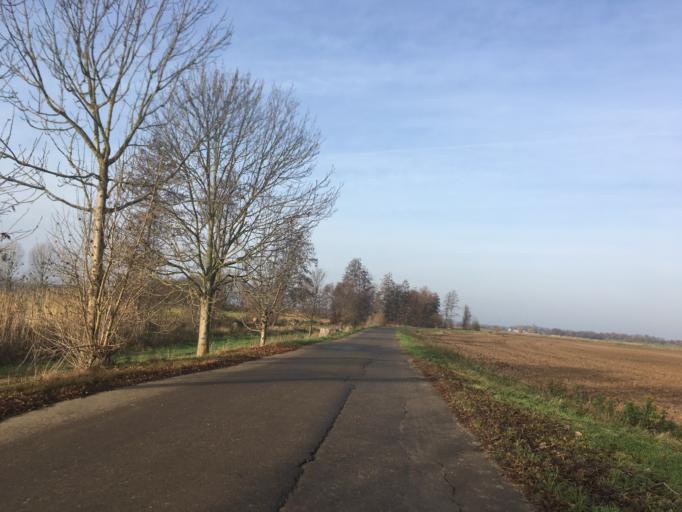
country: DE
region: Brandenburg
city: Wriezen
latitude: 52.7621
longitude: 14.1122
